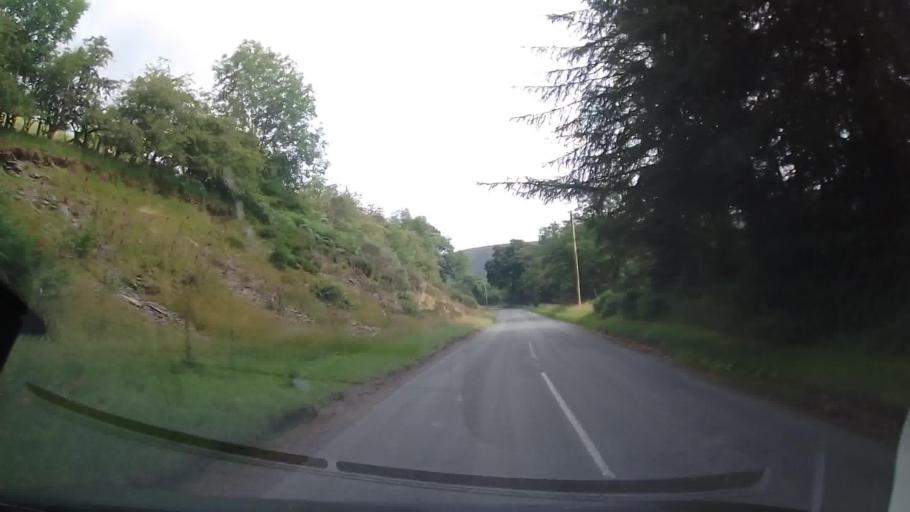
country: GB
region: Wales
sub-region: Sir Powys
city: Llangynog
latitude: 52.8434
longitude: -3.4229
